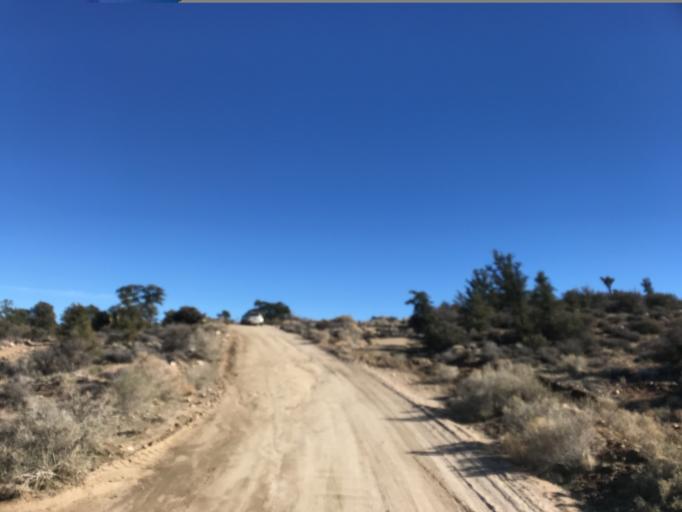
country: US
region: California
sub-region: San Bernardino County
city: Morongo Valley
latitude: 34.2145
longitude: -116.6130
